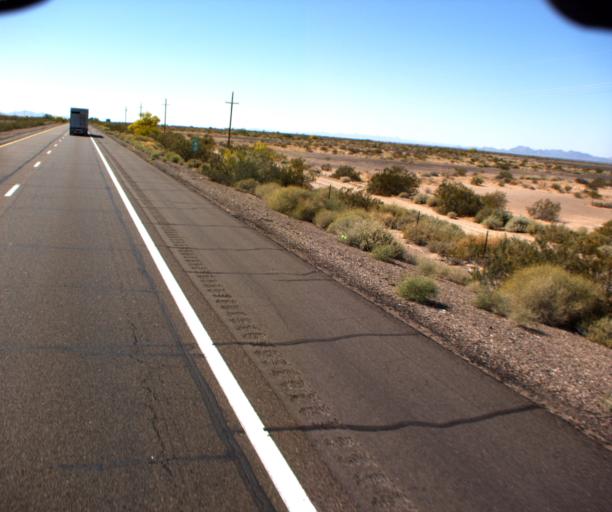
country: US
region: Arizona
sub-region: Maricopa County
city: Gila Bend
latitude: 32.8392
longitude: -113.3308
